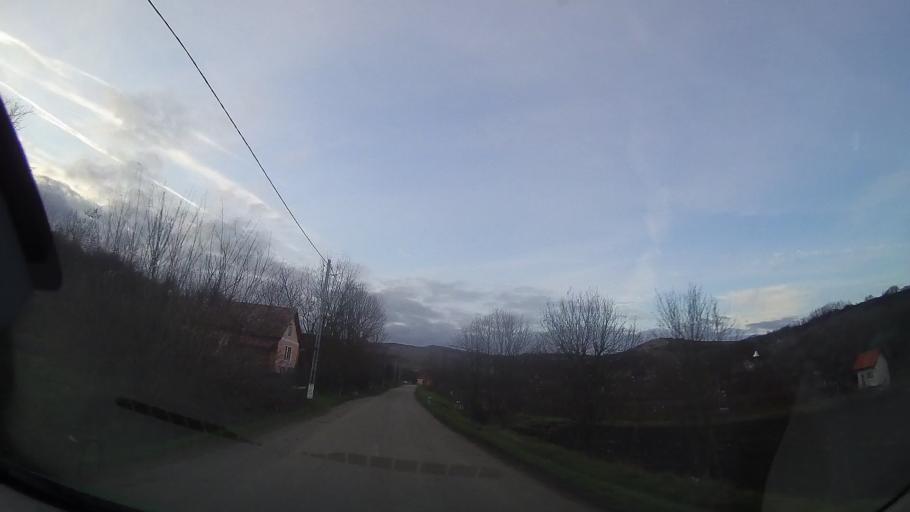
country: RO
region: Cluj
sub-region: Comuna Geaca
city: Geaca
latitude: 46.8530
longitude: 24.0496
